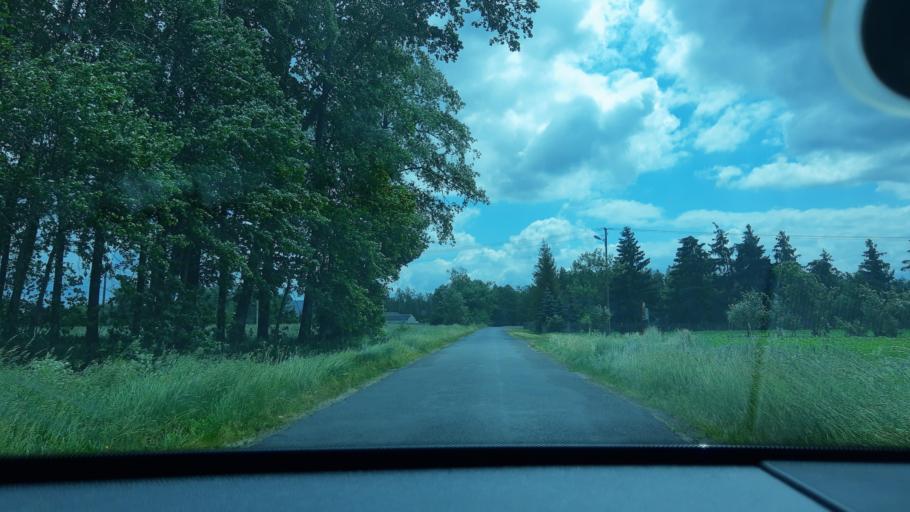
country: PL
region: Lodz Voivodeship
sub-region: Powiat zdunskowolski
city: Zapolice
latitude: 51.5351
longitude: 18.8340
